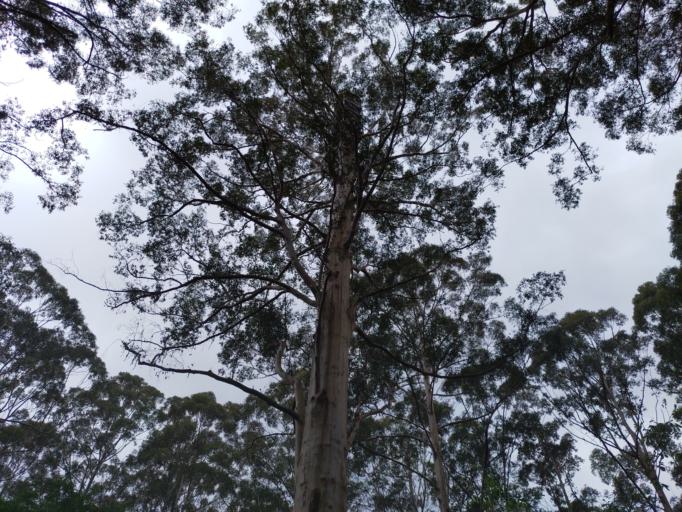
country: AU
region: Western Australia
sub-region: Manjimup
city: Pemberton
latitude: -34.4477
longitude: 116.0573
